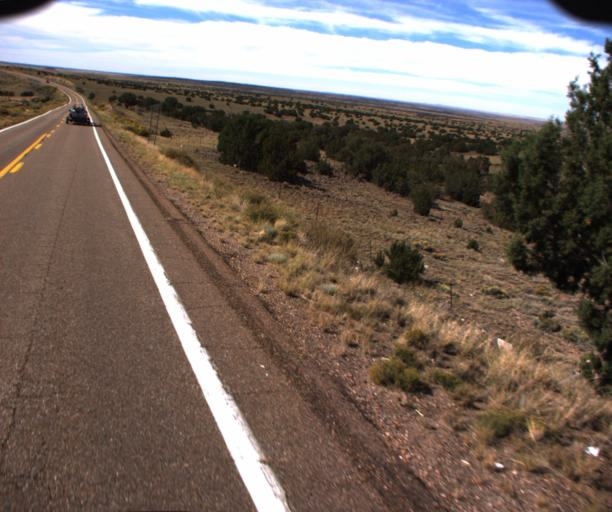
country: US
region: Arizona
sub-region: Apache County
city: Saint Johns
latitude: 34.4841
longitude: -109.5732
